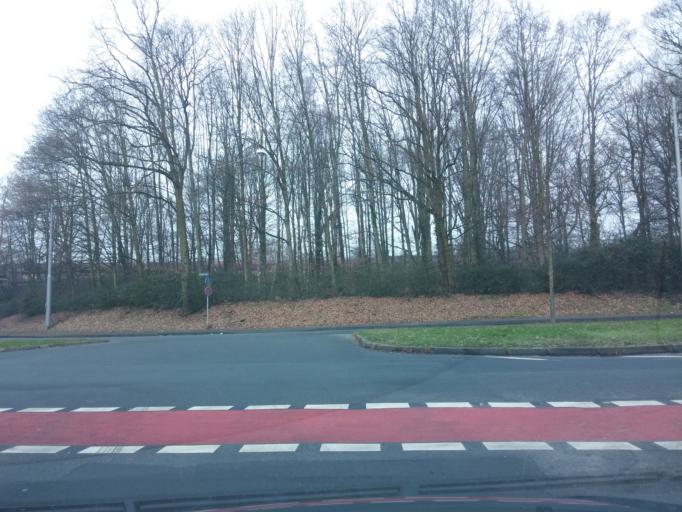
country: DE
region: North Rhine-Westphalia
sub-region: Regierungsbezirk Munster
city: Gladbeck
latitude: 51.5676
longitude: 6.9719
